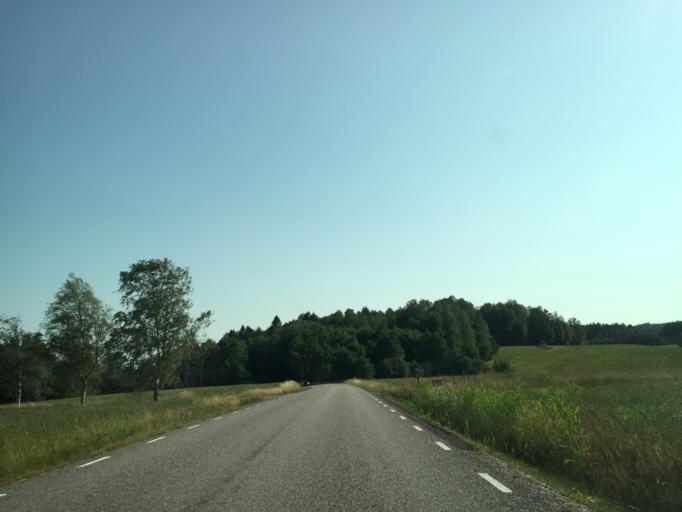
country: SE
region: Vaestra Goetaland
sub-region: Trollhattan
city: Sjuntorp
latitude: 58.2240
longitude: 12.1474
